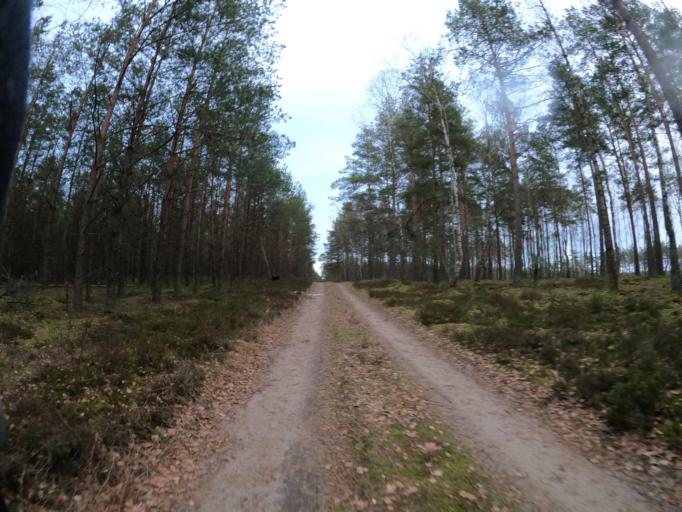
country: PL
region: West Pomeranian Voivodeship
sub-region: Powiat szczecinecki
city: Borne Sulinowo
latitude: 53.5589
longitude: 16.5684
